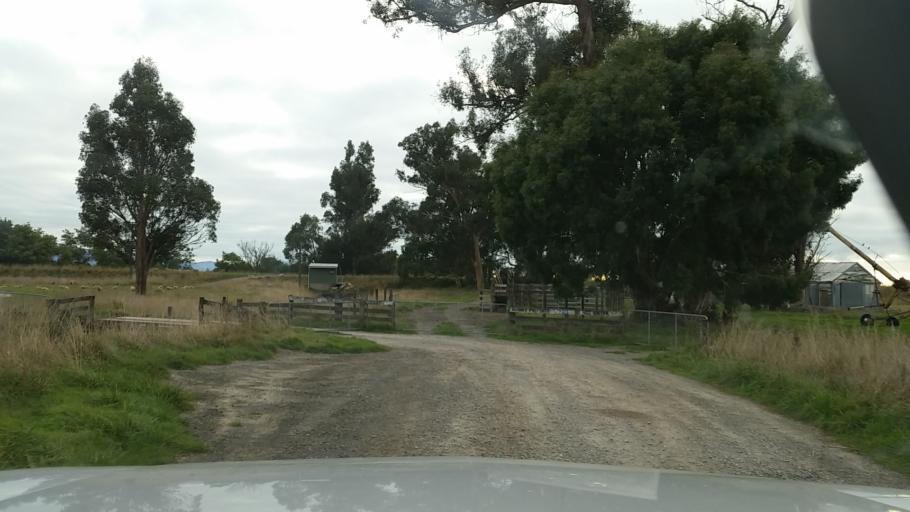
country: NZ
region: Marlborough
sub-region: Marlborough District
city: Blenheim
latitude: -41.5006
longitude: 174.0338
